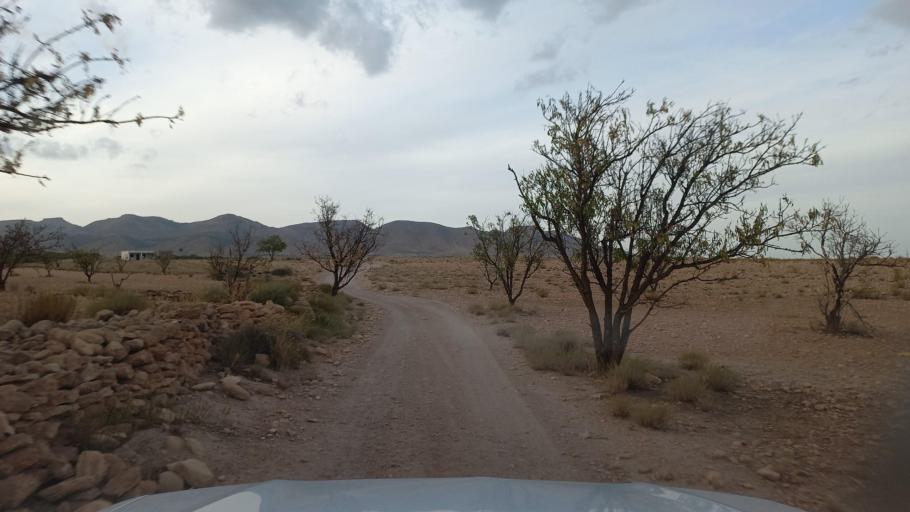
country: TN
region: Al Qasrayn
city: Sbiba
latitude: 35.4228
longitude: 9.0780
